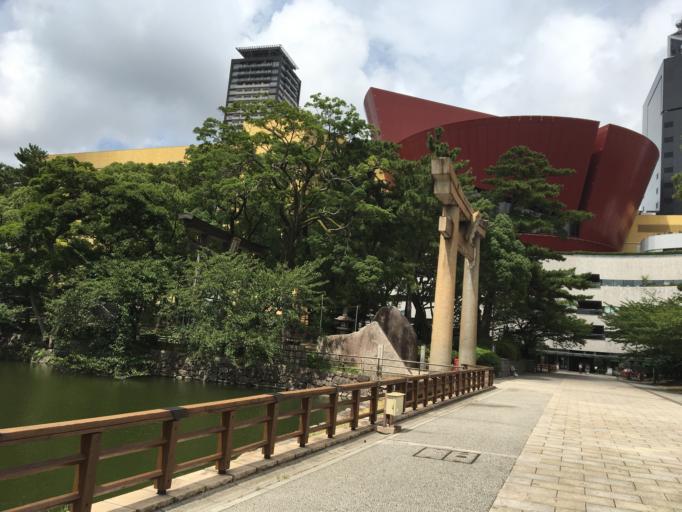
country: JP
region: Fukuoka
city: Kitakyushu
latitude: 33.8844
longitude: 130.8749
